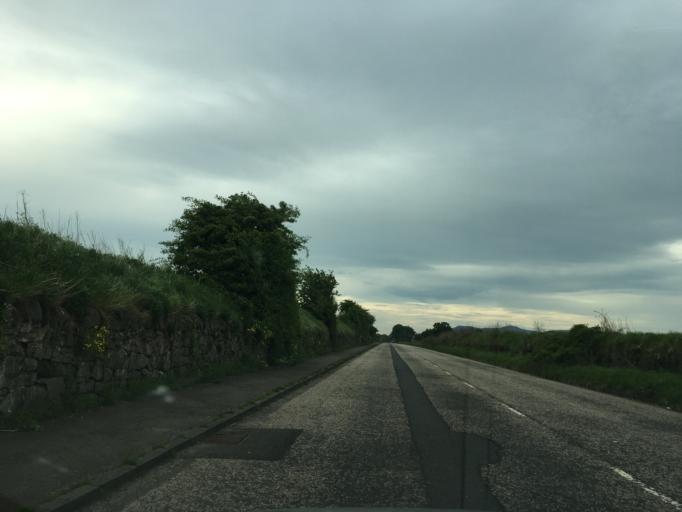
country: GB
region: Scotland
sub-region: Edinburgh
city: Currie
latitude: 55.9482
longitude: -3.3305
